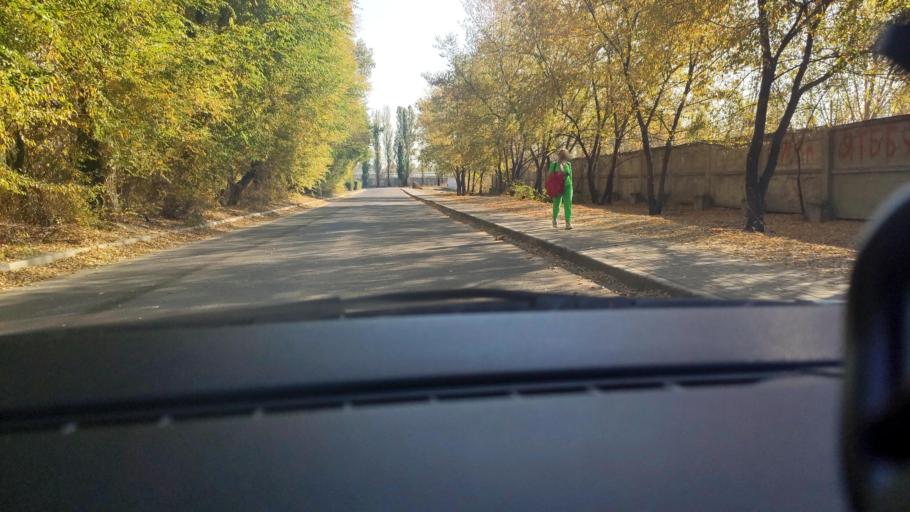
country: RU
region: Voronezj
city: Pridonskoy
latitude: 51.6237
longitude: 39.0688
